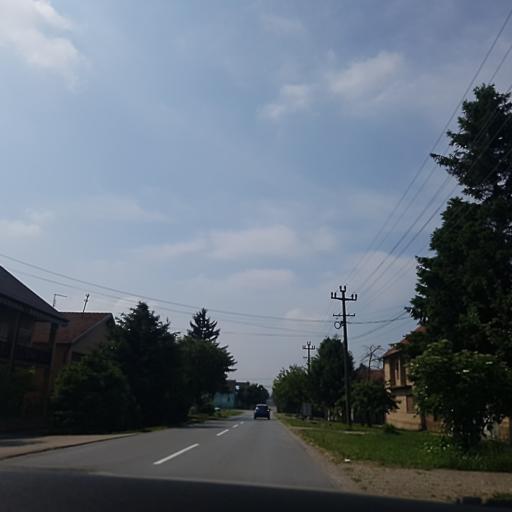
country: RS
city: Padina
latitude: 45.1203
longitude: 20.7217
